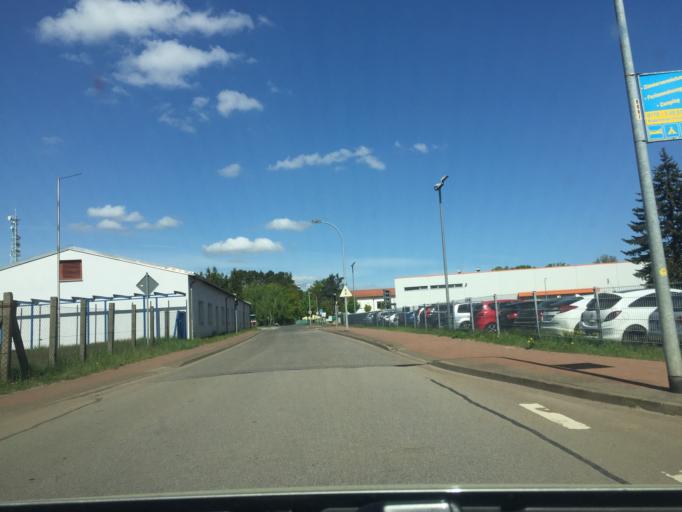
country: DE
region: Mecklenburg-Vorpommern
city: Torgelow
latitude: 53.6338
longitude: 14.0009
